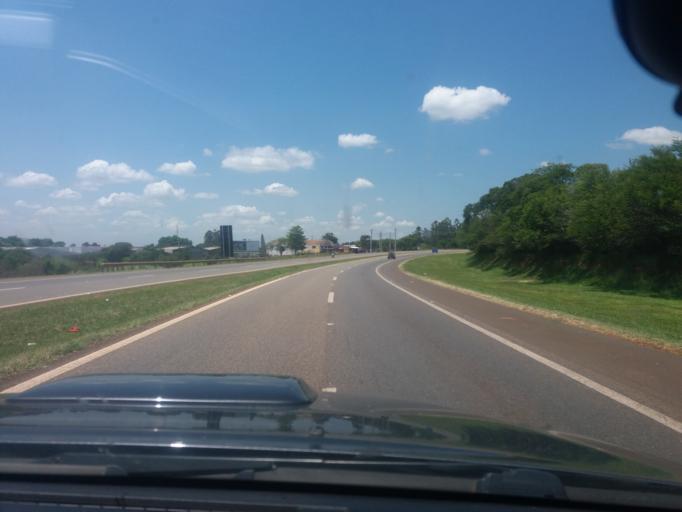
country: BR
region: Sao Paulo
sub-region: Tatui
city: Tatui
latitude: -23.3558
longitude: -47.8808
